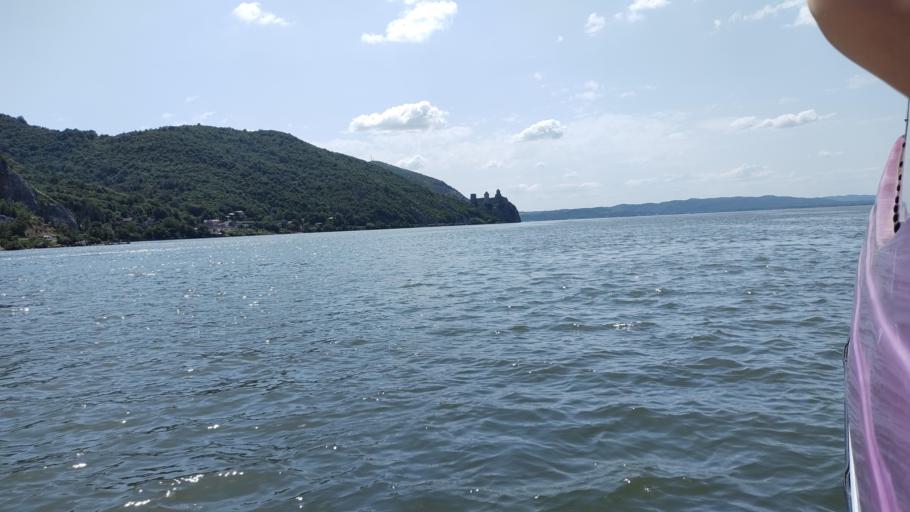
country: RO
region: Caras-Severin
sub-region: Comuna Pescari
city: Coronini
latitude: 44.6637
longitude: 21.6964
